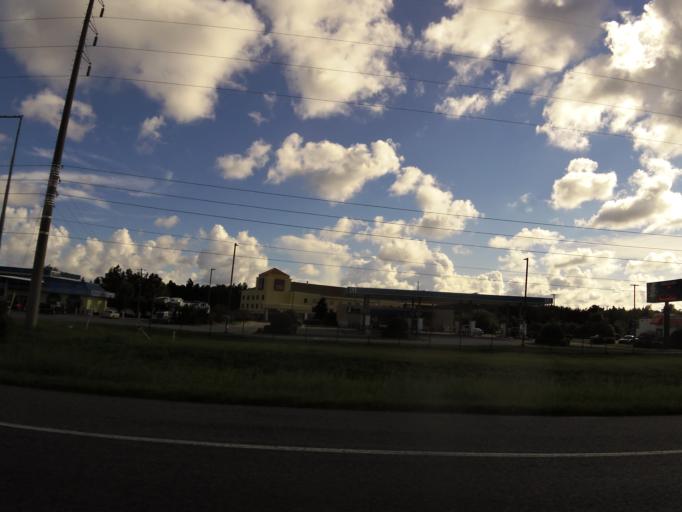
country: US
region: Georgia
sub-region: Glynn County
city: Brunswick
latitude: 31.1363
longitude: -81.5717
